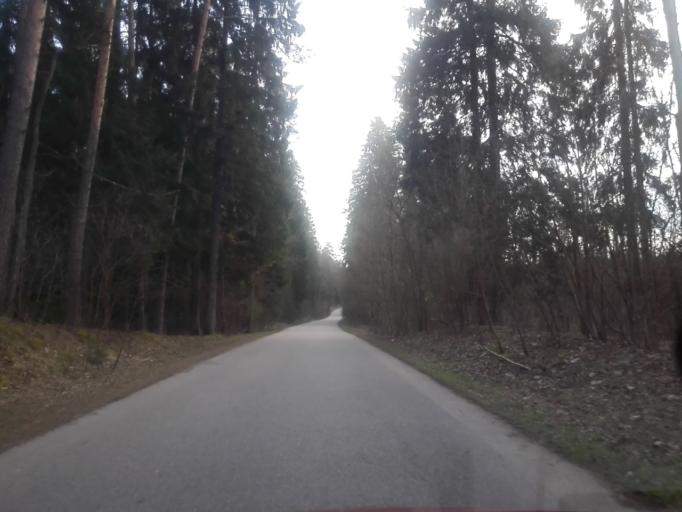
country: PL
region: Podlasie
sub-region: Powiat sejnenski
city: Sejny
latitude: 54.0305
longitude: 23.3758
